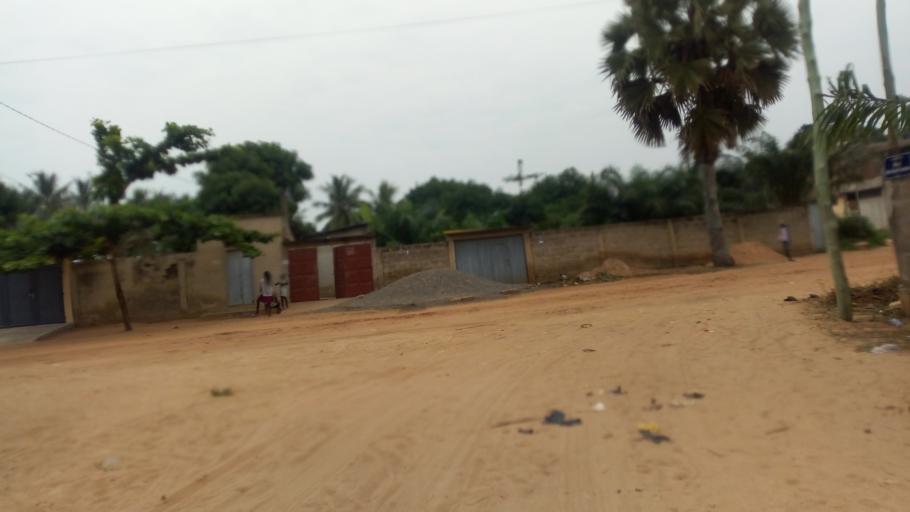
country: TG
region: Maritime
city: Lome
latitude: 6.1713
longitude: 1.1774
